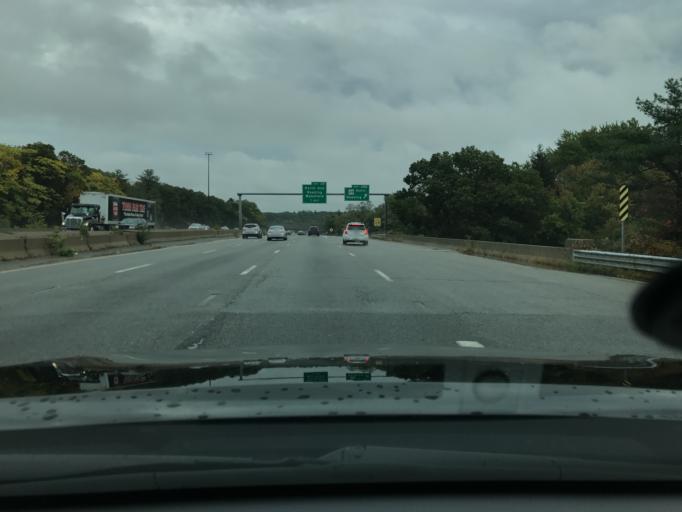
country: US
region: Massachusetts
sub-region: Middlesex County
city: Stoneham
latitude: 42.5033
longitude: -71.1033
